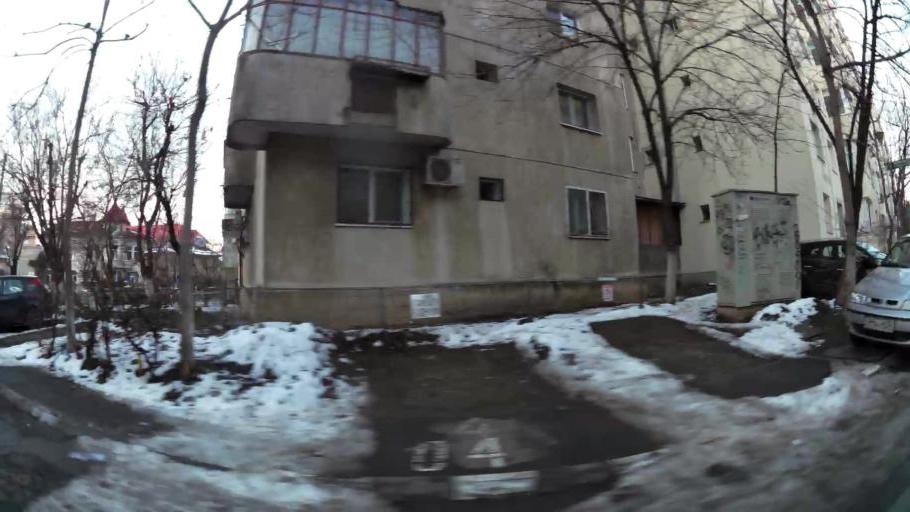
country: RO
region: Ilfov
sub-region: Comuna Fundeni-Dobroesti
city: Fundeni
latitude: 44.4455
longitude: 26.1429
